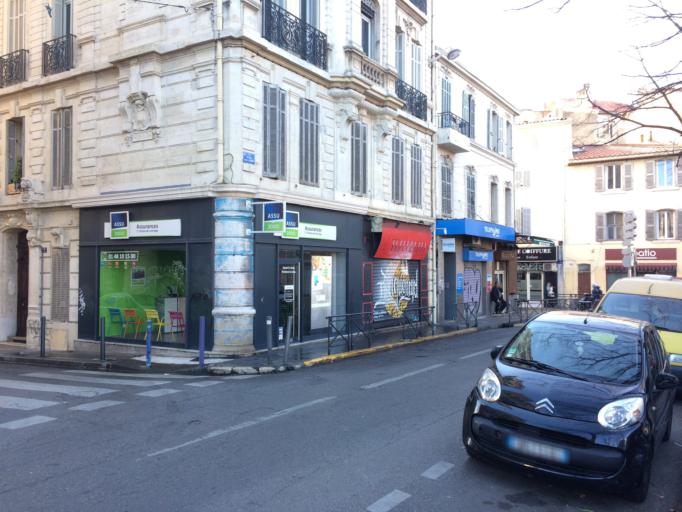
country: FR
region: Provence-Alpes-Cote d'Azur
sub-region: Departement des Bouches-du-Rhone
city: Marseille 01
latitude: 43.2943
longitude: 5.3868
